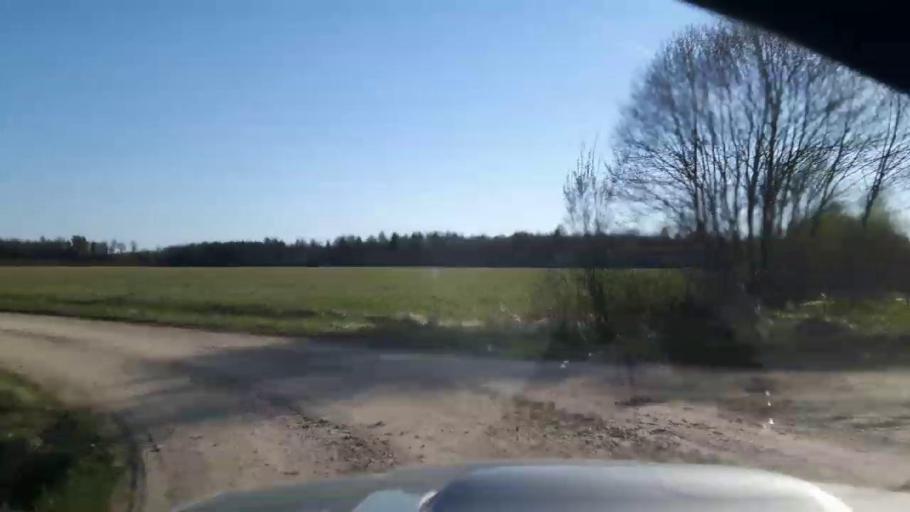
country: EE
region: Paernumaa
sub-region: Tootsi vald
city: Tootsi
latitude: 58.4335
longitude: 24.8512
